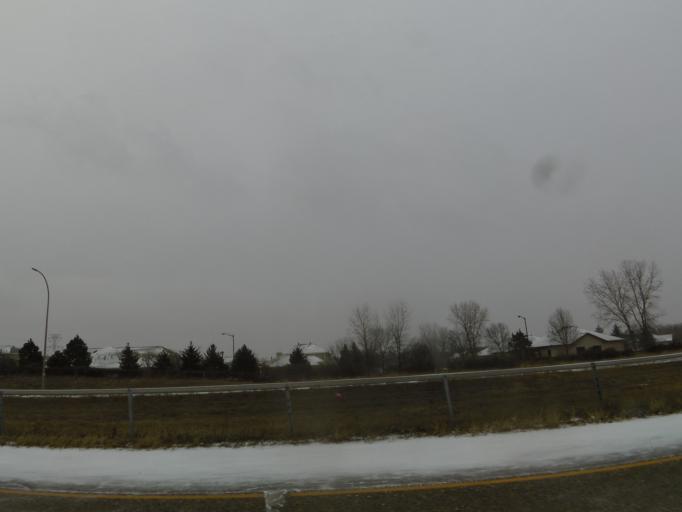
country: US
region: Minnesota
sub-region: Dakota County
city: Eagan
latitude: 44.7950
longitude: -93.2223
